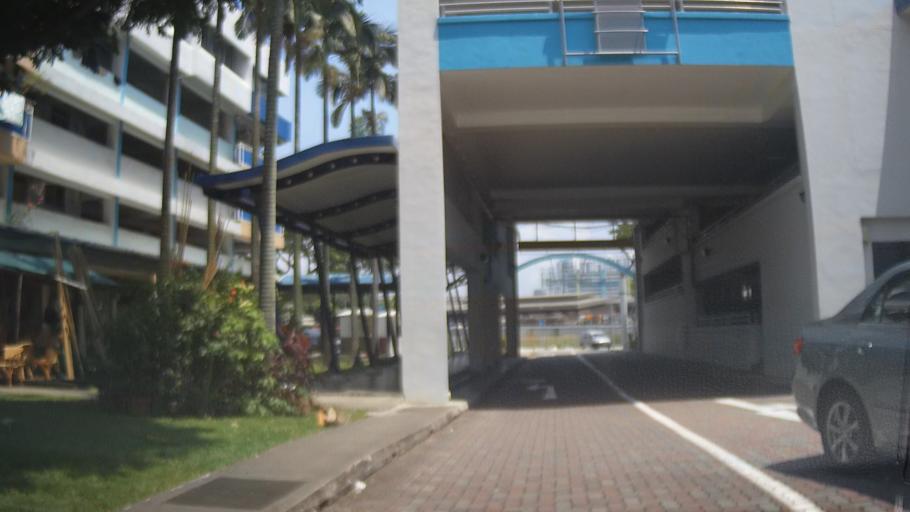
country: SG
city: Singapore
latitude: 1.3206
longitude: 103.8692
